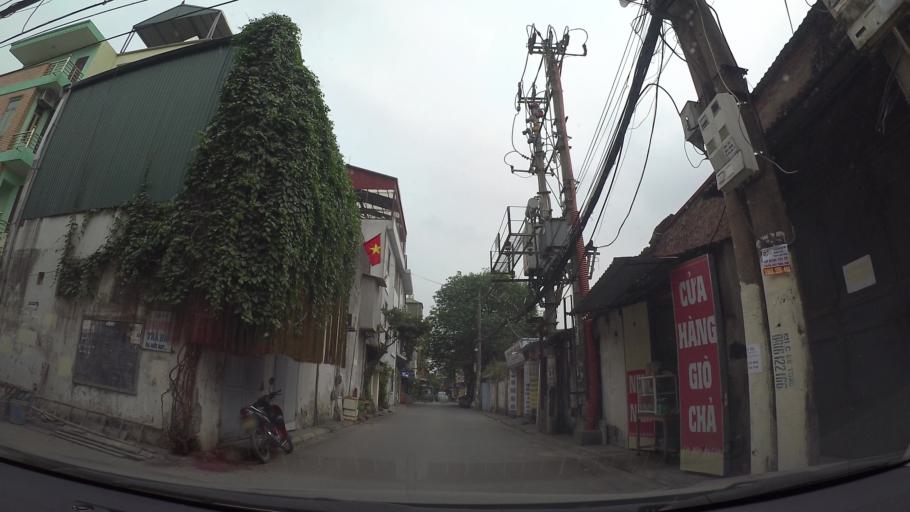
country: VN
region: Ha Noi
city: Hoan Kiem
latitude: 21.0661
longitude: 105.8830
